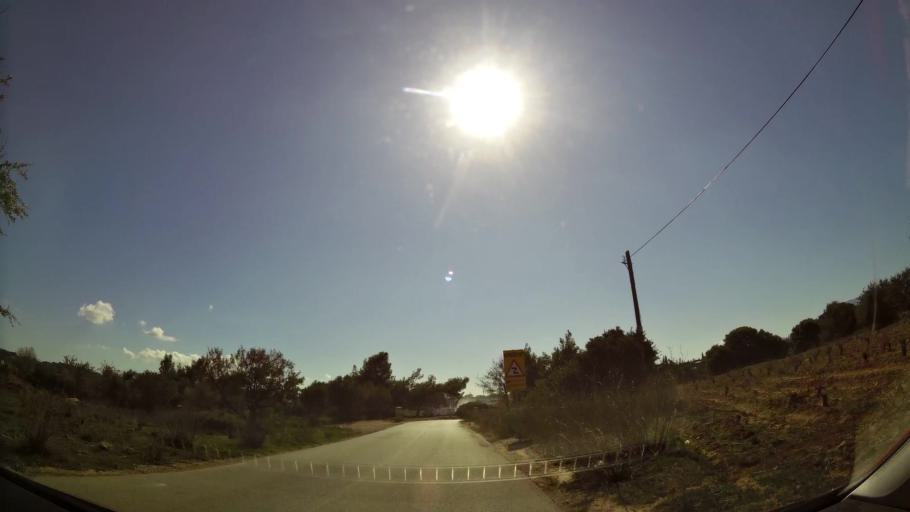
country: GR
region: Attica
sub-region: Nomarchia Anatolikis Attikis
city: Pikermi
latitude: 38.0082
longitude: 23.9423
